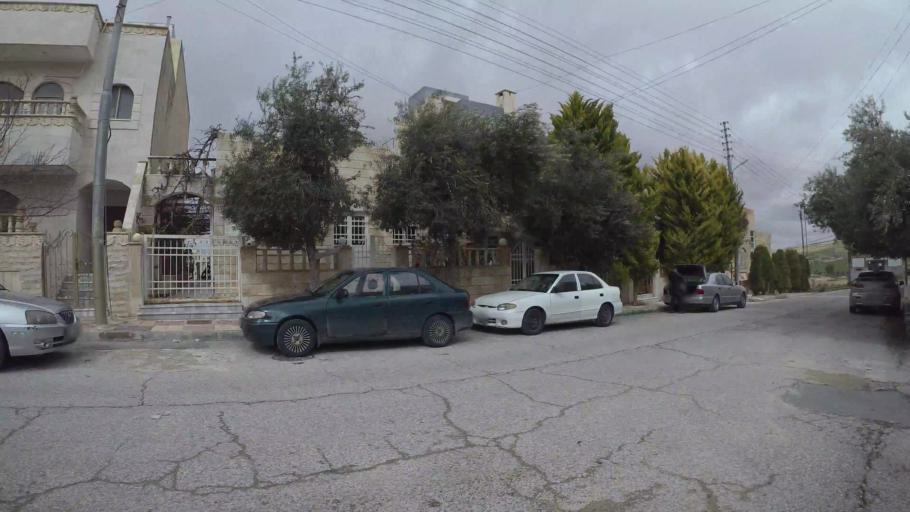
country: JO
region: Amman
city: Al Jubayhah
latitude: 32.0695
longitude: 35.8836
